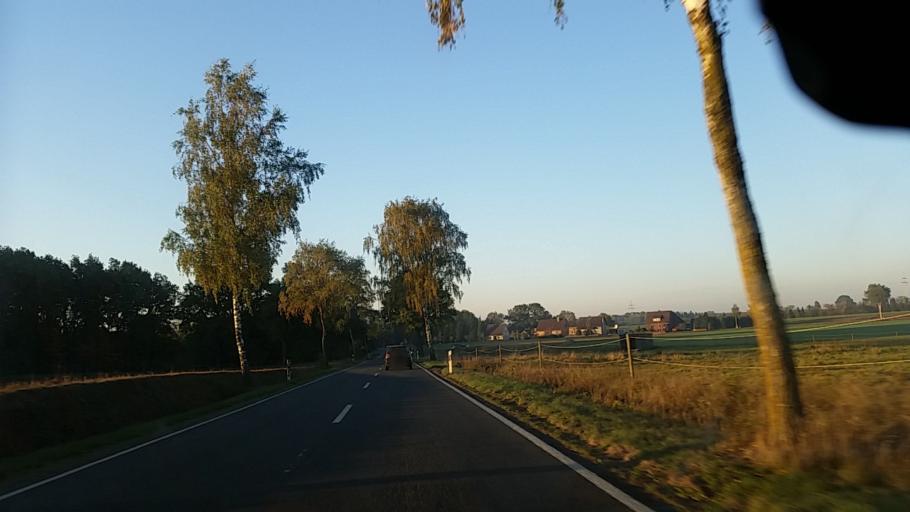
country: DE
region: Lower Saxony
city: Wittingen
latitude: 52.6769
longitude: 10.8006
